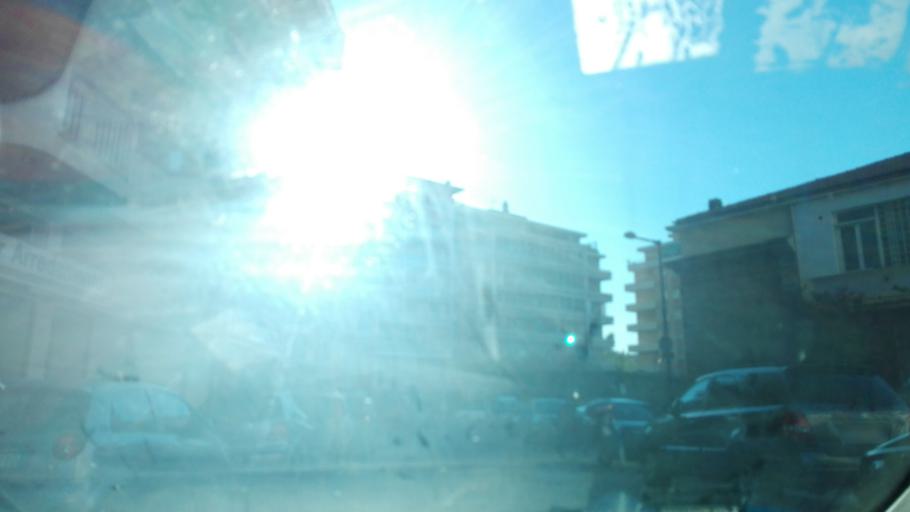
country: IT
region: Abruzzo
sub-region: Provincia di Pescara
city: Pescara
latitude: 42.4733
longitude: 14.2026
